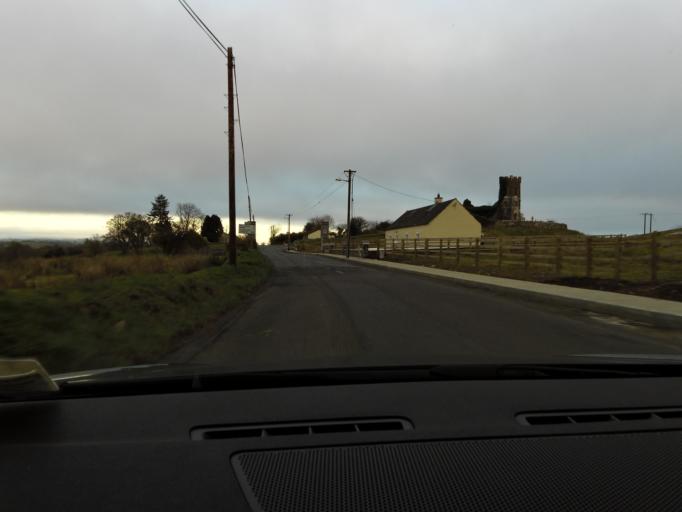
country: IE
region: Connaught
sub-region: Sligo
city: Ballymote
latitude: 53.9915
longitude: -8.5119
